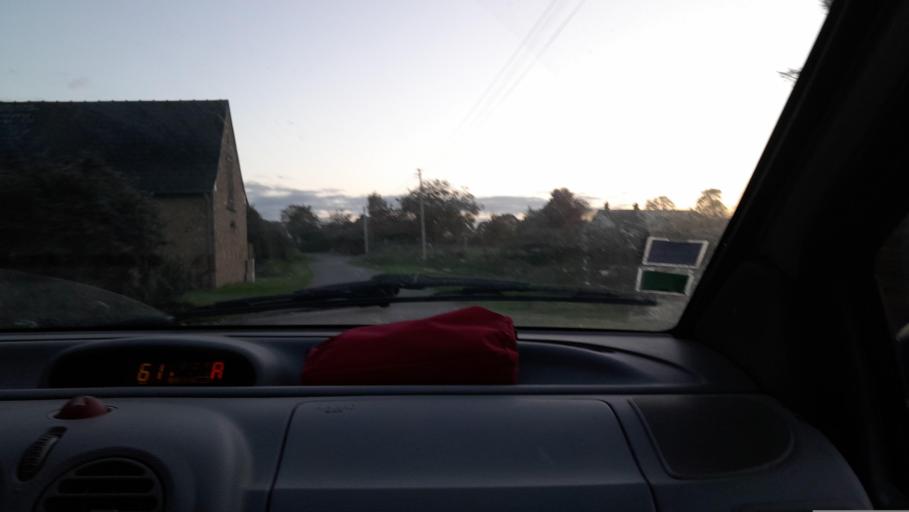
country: FR
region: Brittany
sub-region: Departement d'Ille-et-Vilaine
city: Rannee
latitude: 47.8789
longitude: -1.1836
